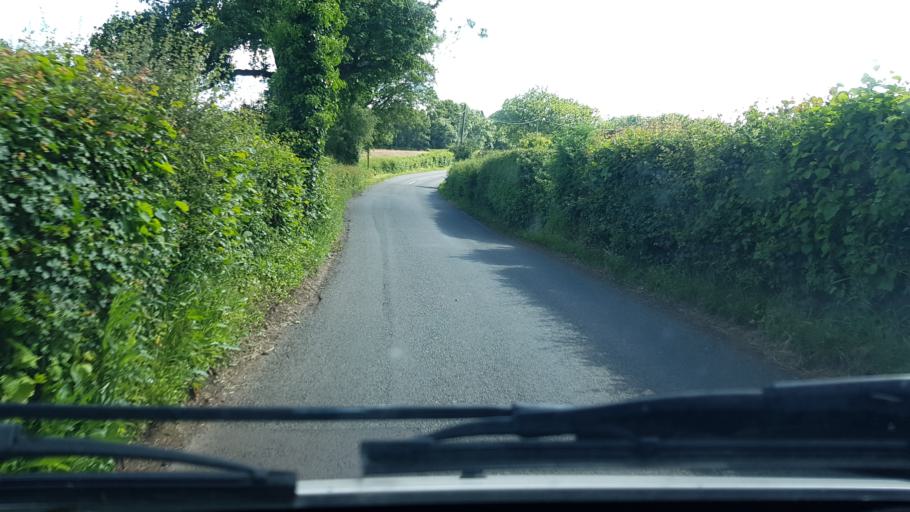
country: GB
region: England
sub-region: Worcestershire
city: Bewdley
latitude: 52.4103
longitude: -2.3076
